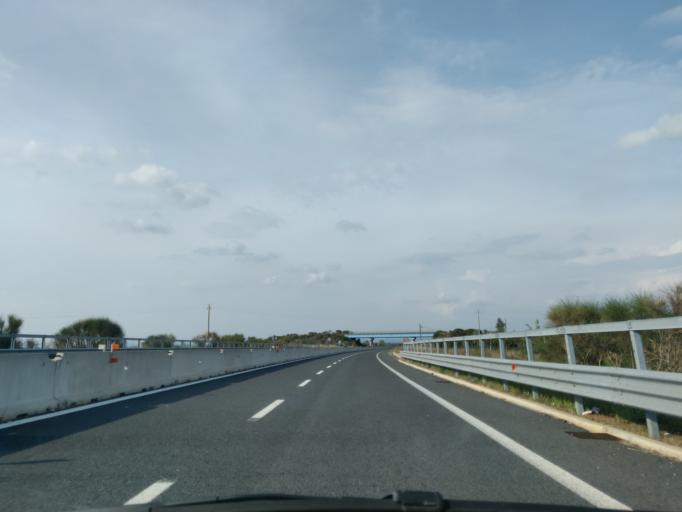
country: IT
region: Latium
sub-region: Provincia di Viterbo
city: Blera
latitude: 42.3484
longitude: 11.9813
